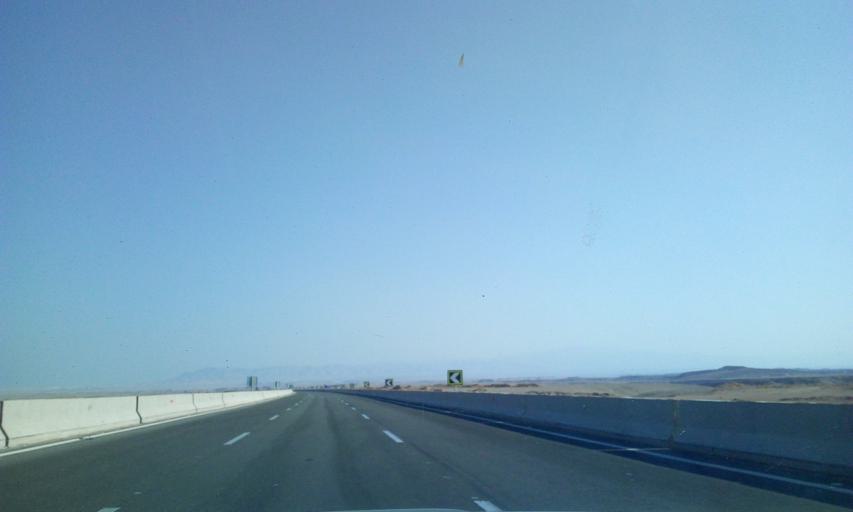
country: EG
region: As Suways
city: Ain Sukhna
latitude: 29.2035
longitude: 32.4942
